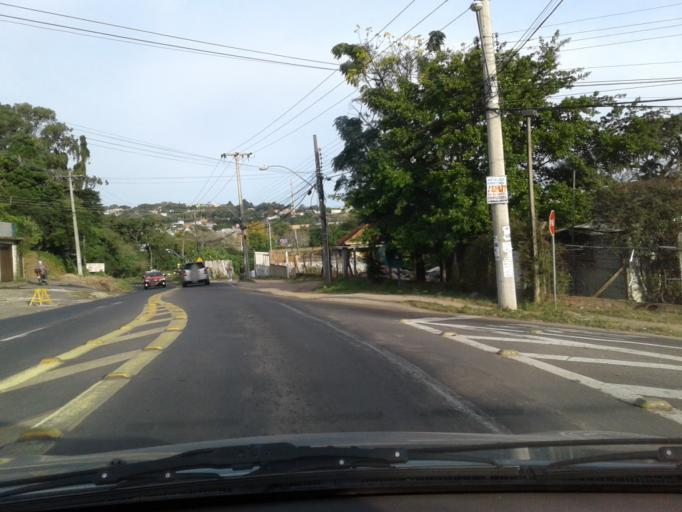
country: BR
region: Rio Grande do Sul
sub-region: Porto Alegre
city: Porto Alegre
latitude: -30.1006
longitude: -51.2250
